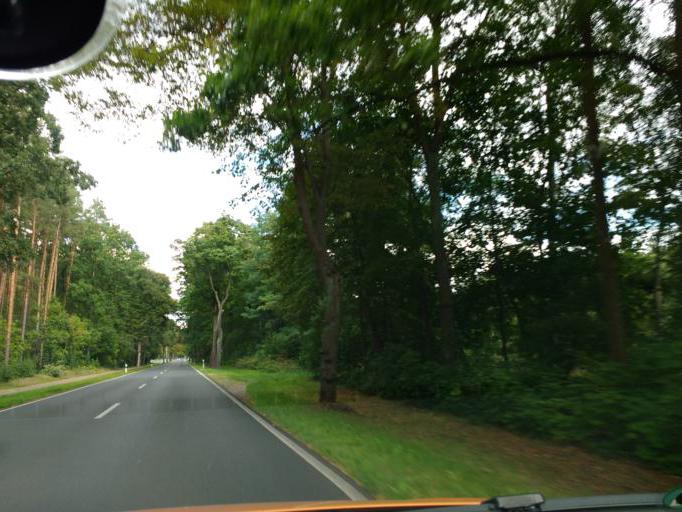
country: DE
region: Brandenburg
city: Wandlitz
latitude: 52.8056
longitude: 13.4890
